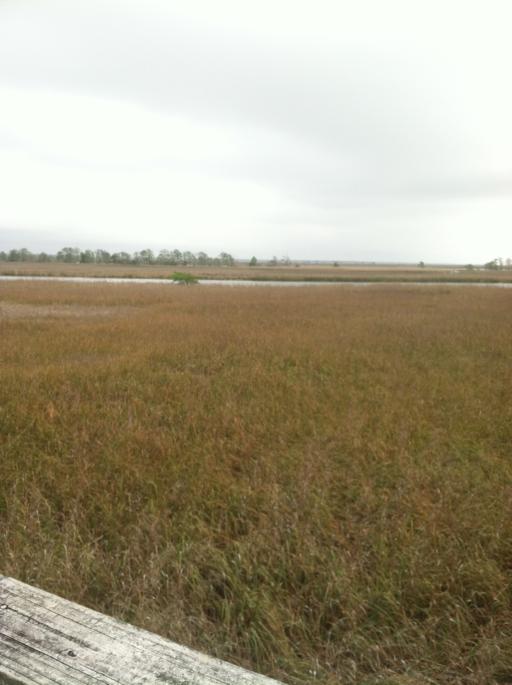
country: US
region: Florida
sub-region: Franklin County
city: Apalachicola
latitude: 29.7350
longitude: -84.9980
